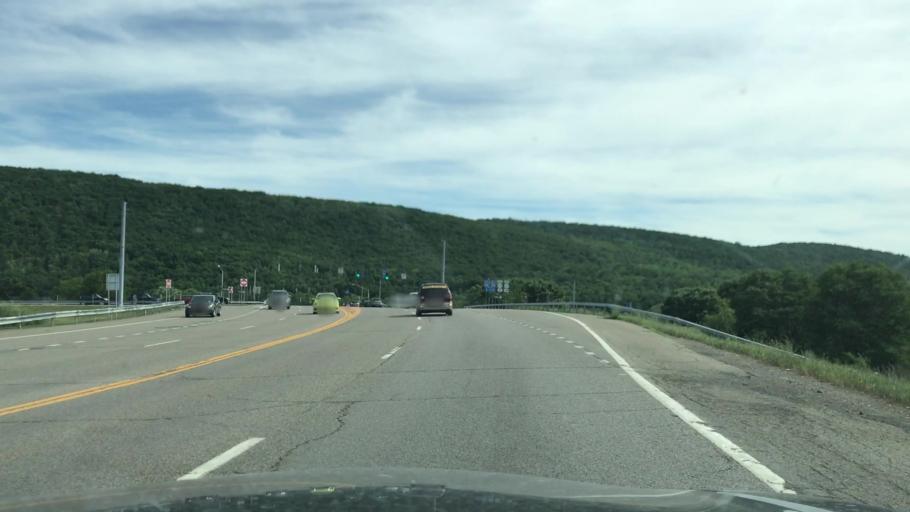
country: US
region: New York
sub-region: Chemung County
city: Horseheads
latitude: 42.1587
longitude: -76.8783
